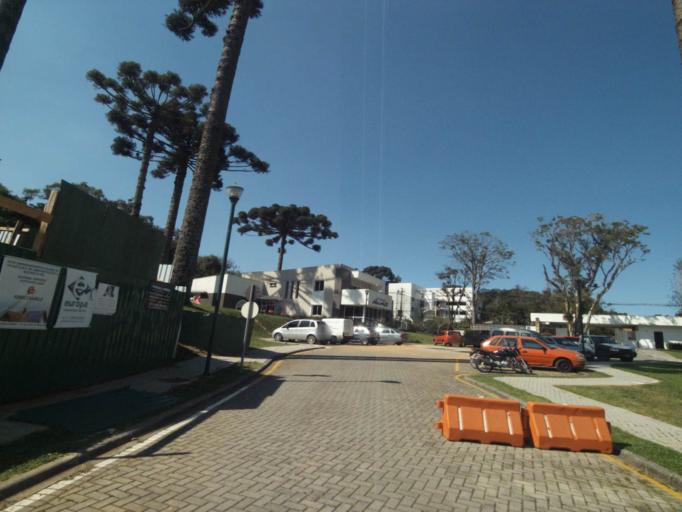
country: BR
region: Parana
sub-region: Curitiba
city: Curitiba
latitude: -25.3834
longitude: -49.2824
